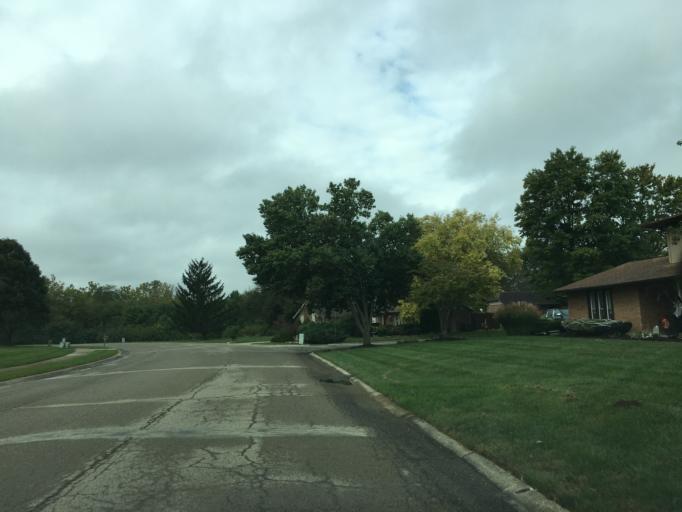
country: US
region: Ohio
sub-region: Butler County
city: Beckett Ridge
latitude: 39.3559
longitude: -84.4487
